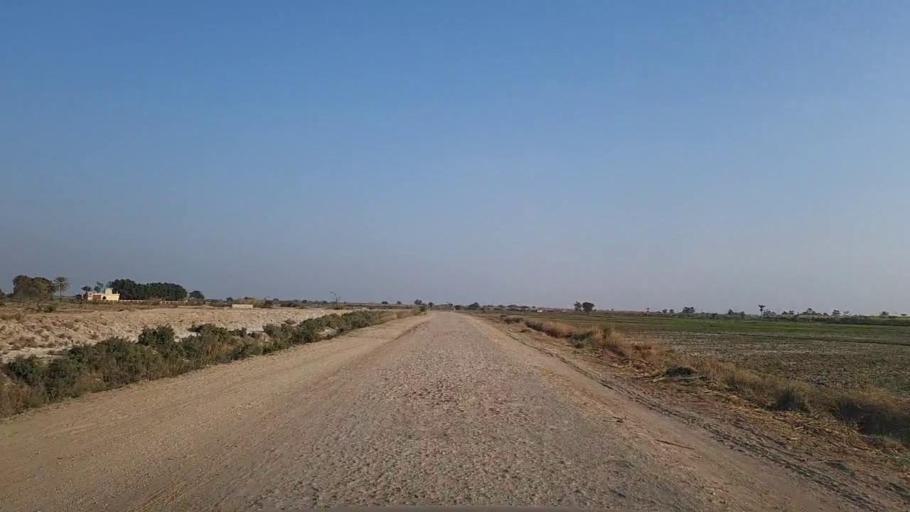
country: PK
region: Sindh
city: Tando Mittha Khan
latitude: 25.9406
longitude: 69.0745
